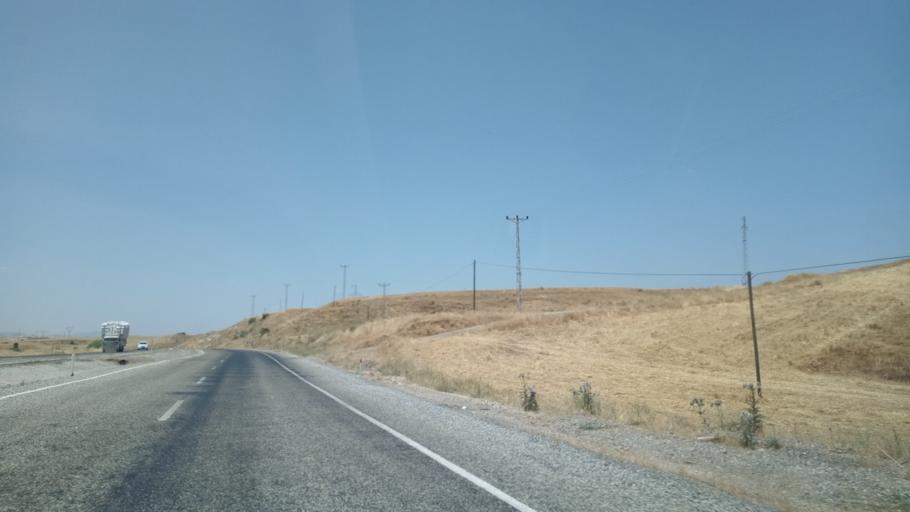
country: TR
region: Batman
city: Bekirhan
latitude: 38.1574
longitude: 41.3462
